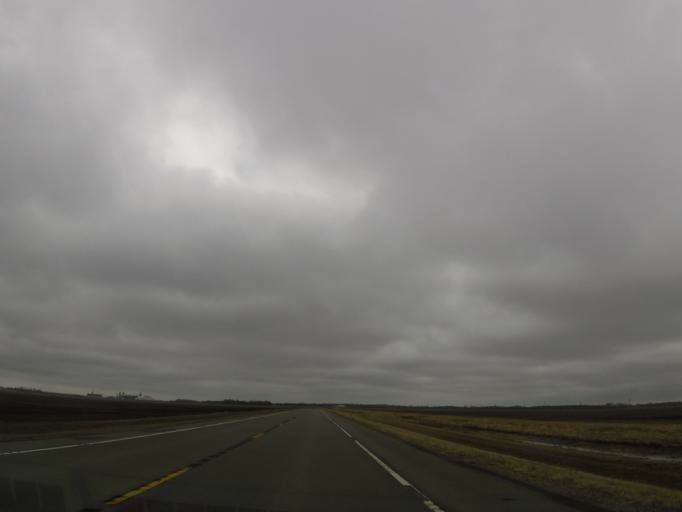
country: US
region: North Dakota
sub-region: Cass County
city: Horace
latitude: 46.6299
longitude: -97.0500
